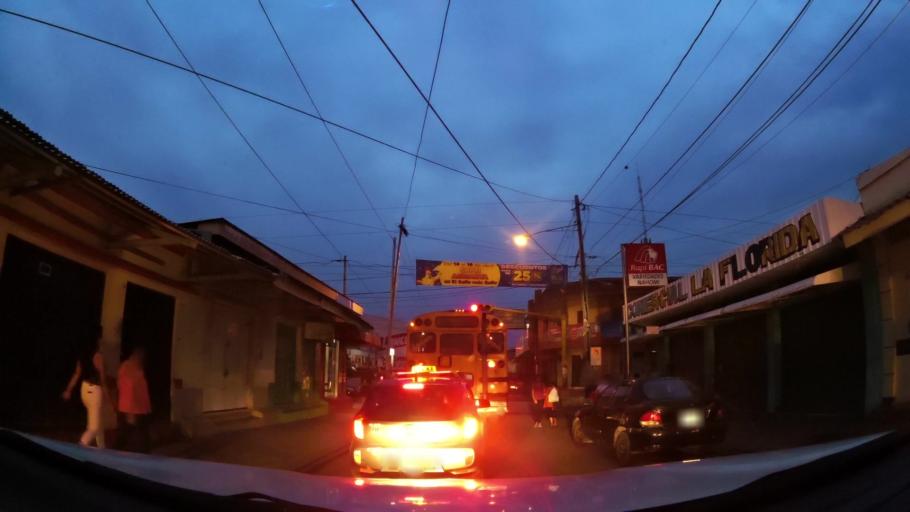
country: NI
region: Esteli
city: Esteli
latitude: 13.0871
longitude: -86.3564
